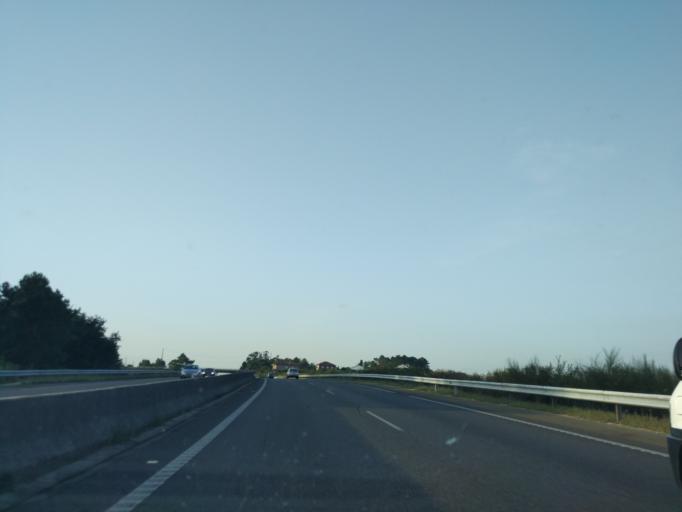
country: ES
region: Galicia
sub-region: Provincia de Pontevedra
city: Caldas de Reis
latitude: 42.6453
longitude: -8.6522
